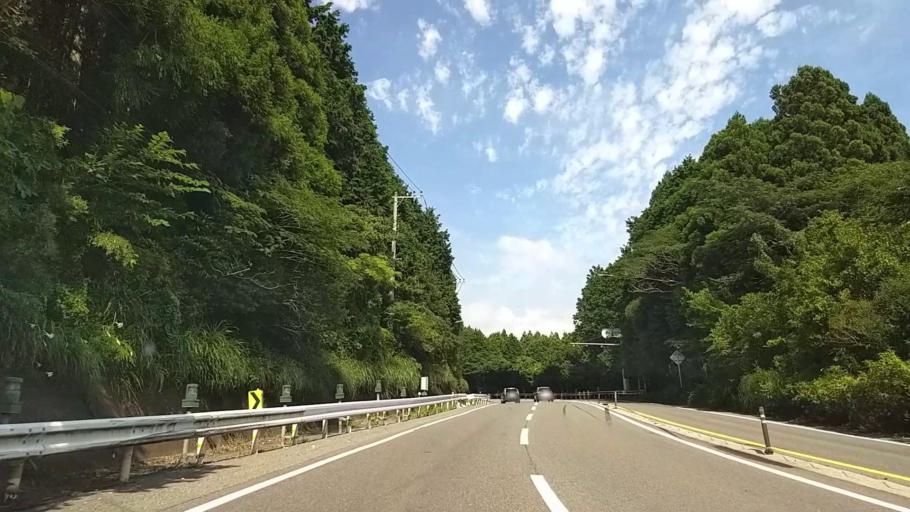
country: JP
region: Kanagawa
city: Hakone
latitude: 35.1602
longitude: 138.9969
